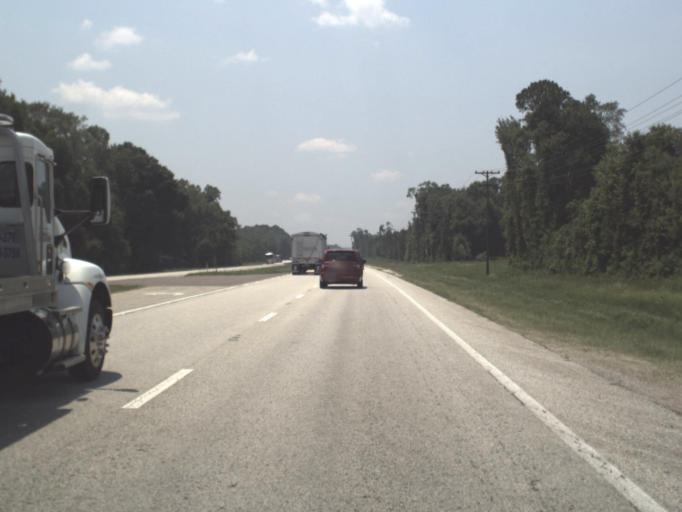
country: US
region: Florida
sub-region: Duval County
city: Baldwin
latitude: 30.1810
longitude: -82.0227
